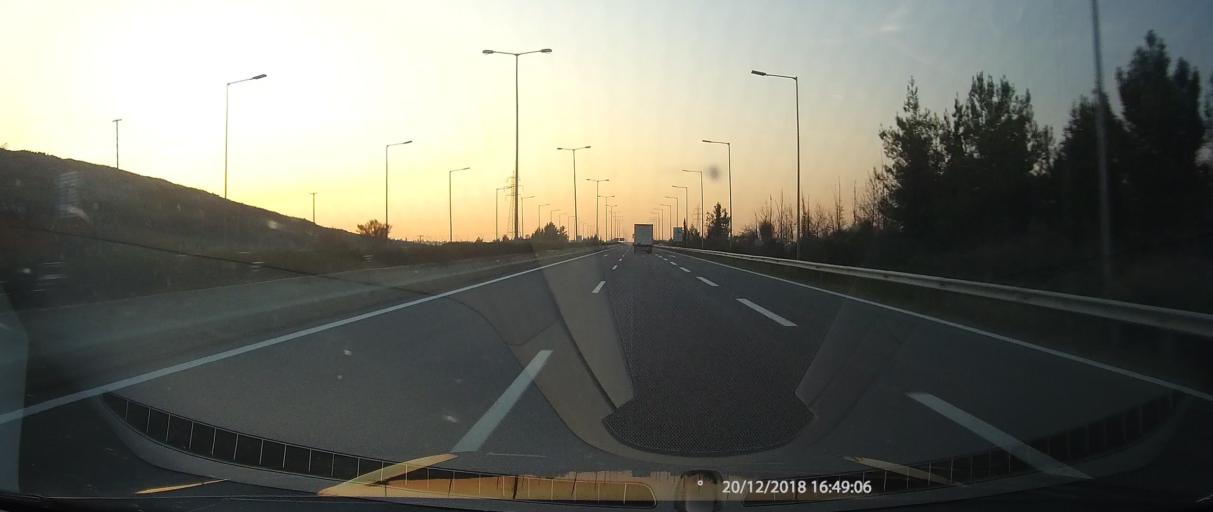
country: GR
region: Thessaly
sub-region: Nomos Larisis
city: Chalki
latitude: 39.4938
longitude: 22.6248
